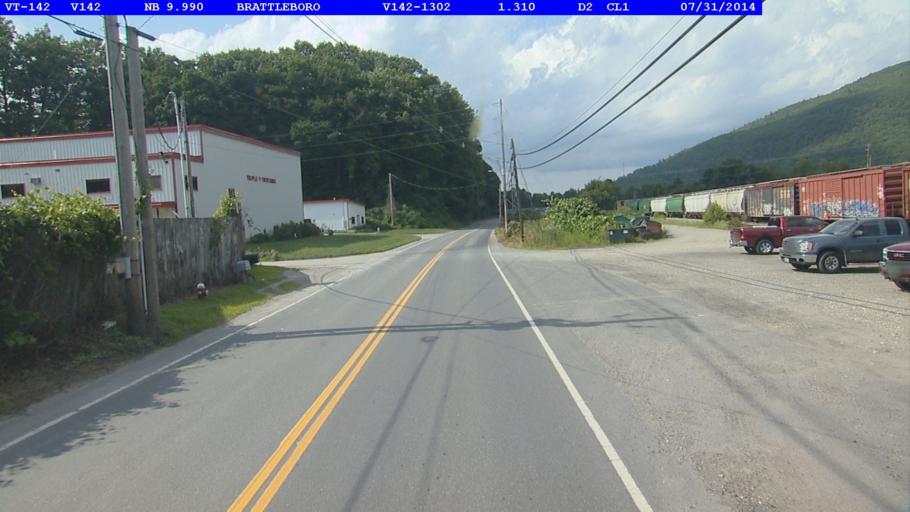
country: US
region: Vermont
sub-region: Windham County
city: Brattleboro
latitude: 42.8401
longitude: -72.5499
